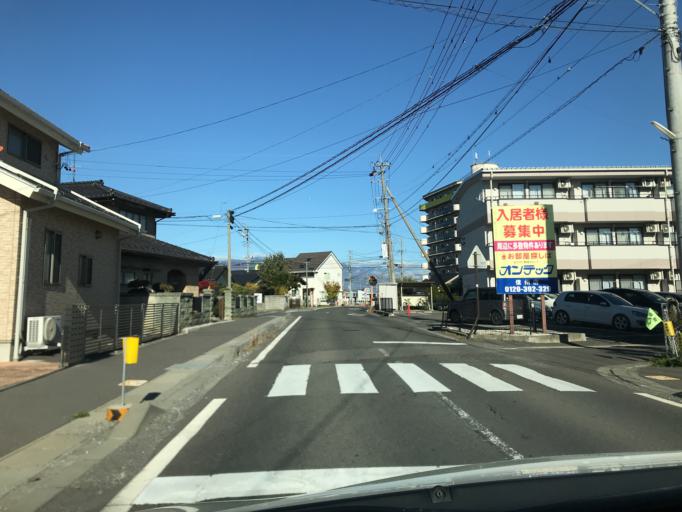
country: JP
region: Nagano
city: Shiojiri
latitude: 36.1174
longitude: 137.9469
